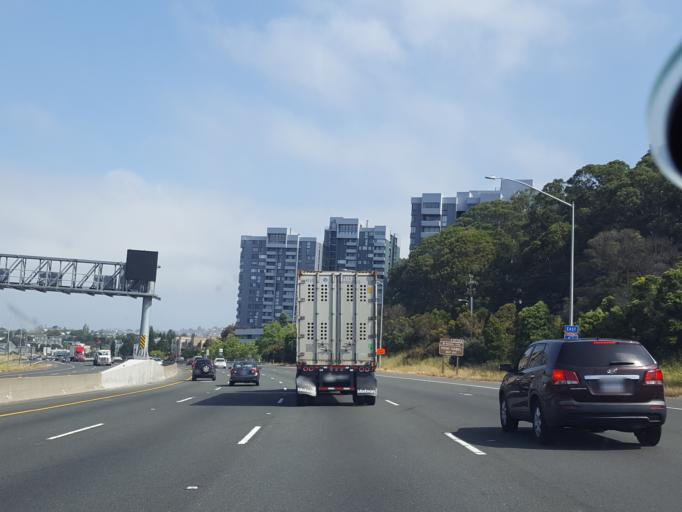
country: US
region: California
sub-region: Alameda County
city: Albany
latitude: 37.8921
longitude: -122.3073
